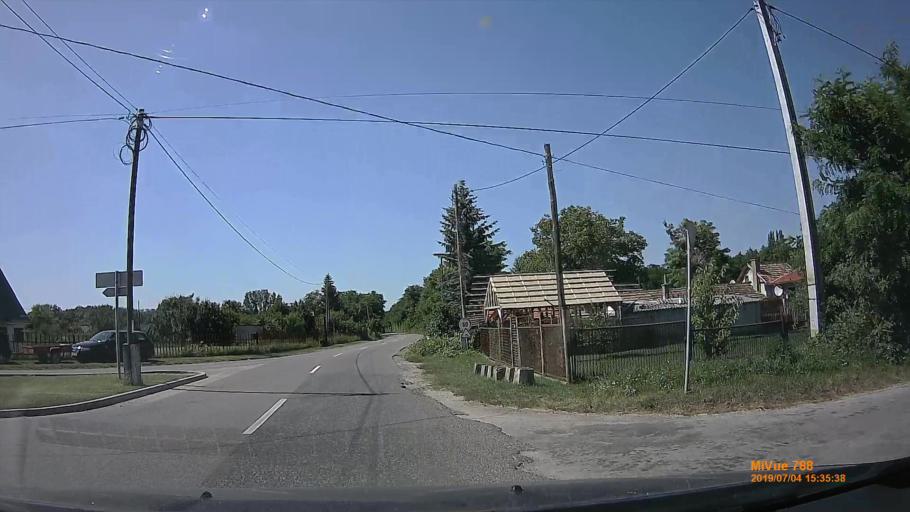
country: HU
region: Komarom-Esztergom
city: Tatabanya
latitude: 47.5422
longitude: 18.3834
